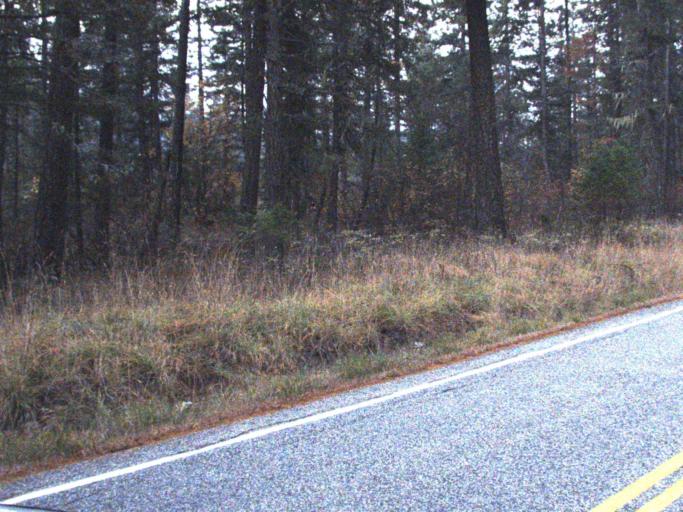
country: CA
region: British Columbia
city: Grand Forks
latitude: 48.9417
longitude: -118.2219
